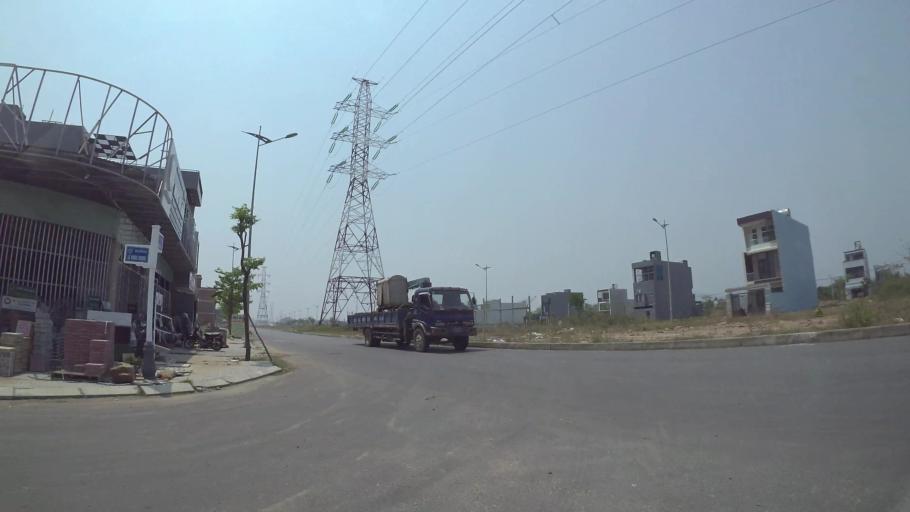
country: VN
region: Da Nang
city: Cam Le
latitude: 16.0159
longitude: 108.2283
